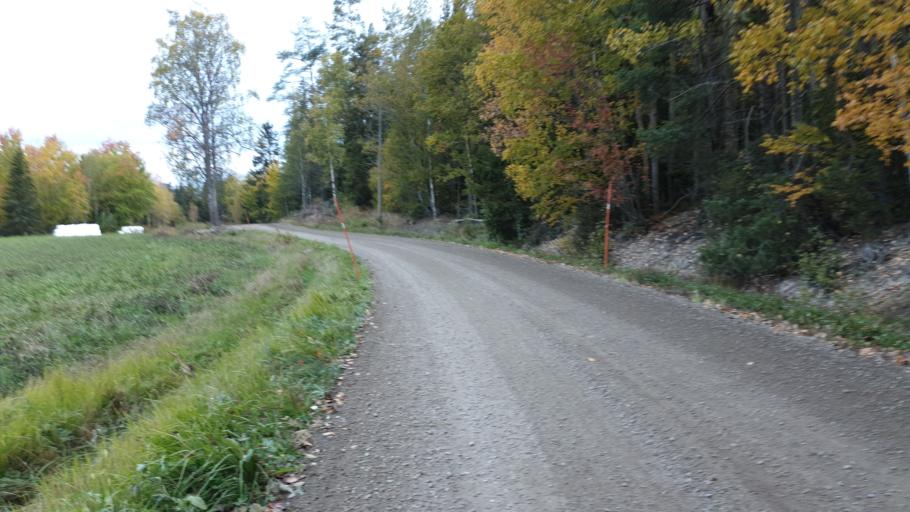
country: SE
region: Vaestmanland
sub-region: Sala Kommun
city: Sala
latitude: 59.8191
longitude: 16.6493
